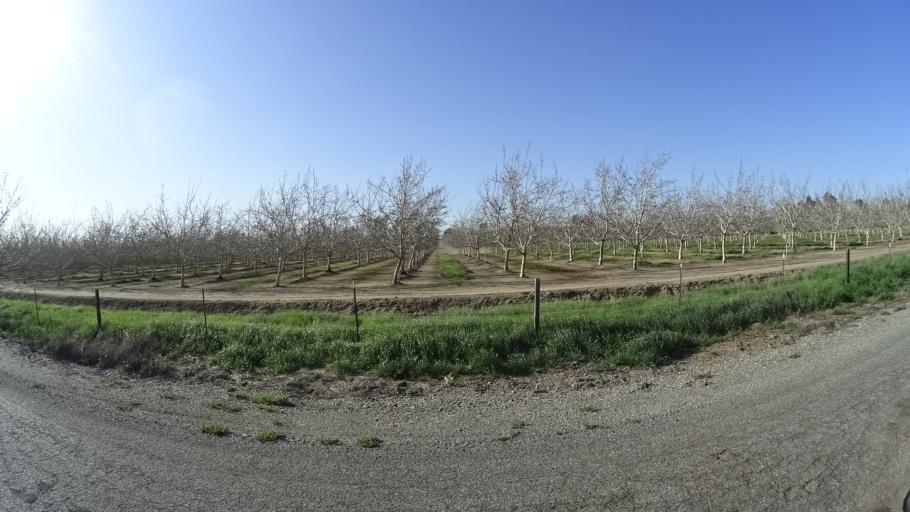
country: US
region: California
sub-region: Glenn County
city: Orland
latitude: 39.7573
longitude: -122.1259
